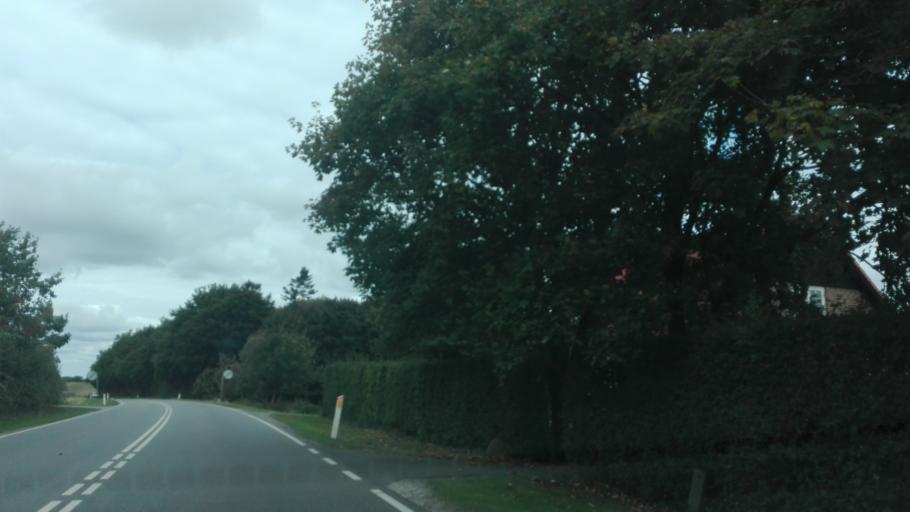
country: DK
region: Central Jutland
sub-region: Skanderborg Kommune
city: Stilling
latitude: 56.0960
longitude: 9.9708
